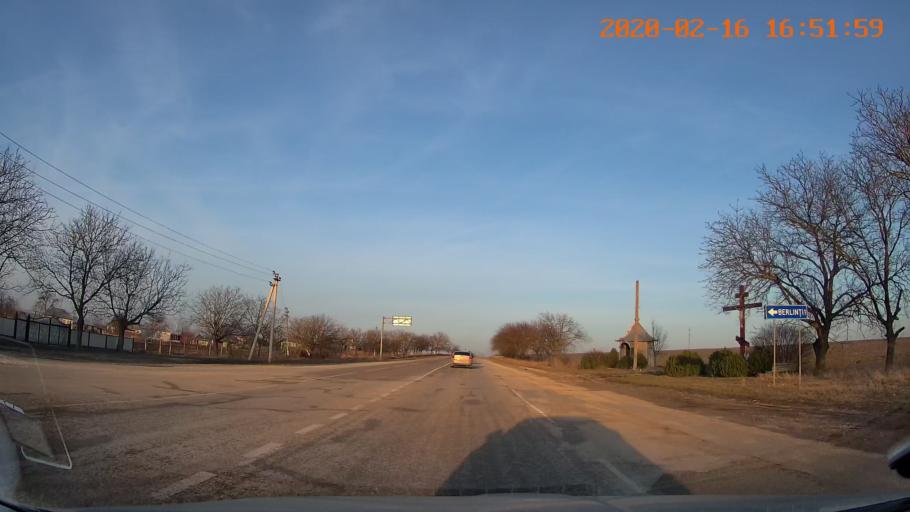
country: MD
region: Briceni
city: Briceni
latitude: 48.3095
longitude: 26.9534
